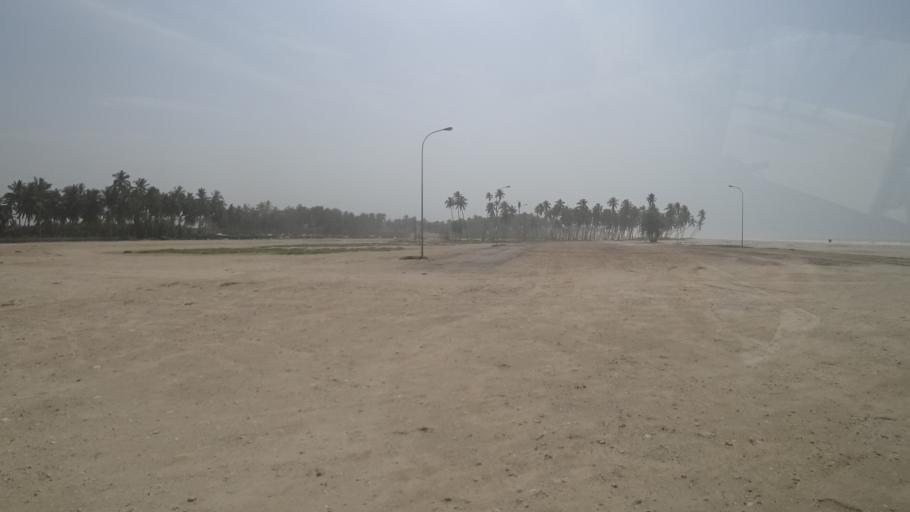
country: OM
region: Zufar
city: Salalah
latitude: 17.0020
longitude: 54.1135
